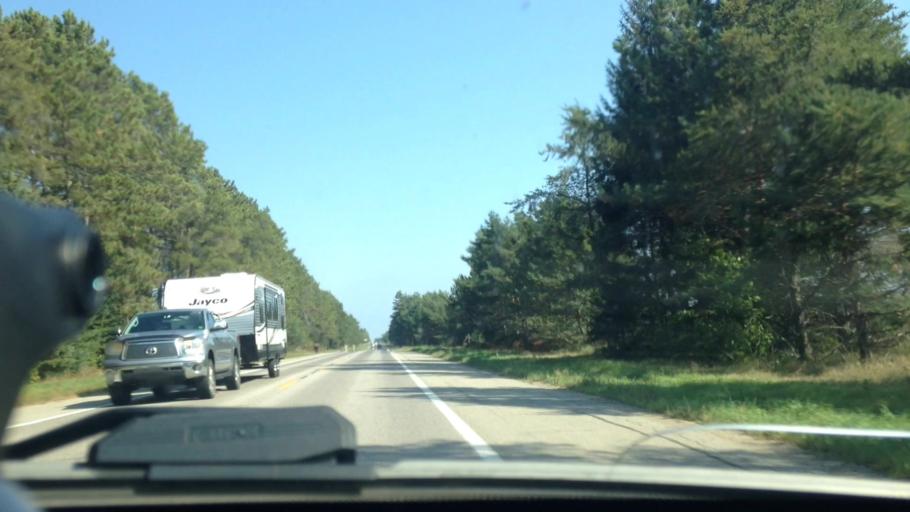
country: US
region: Michigan
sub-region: Luce County
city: Newberry
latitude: 46.3034
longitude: -85.4832
